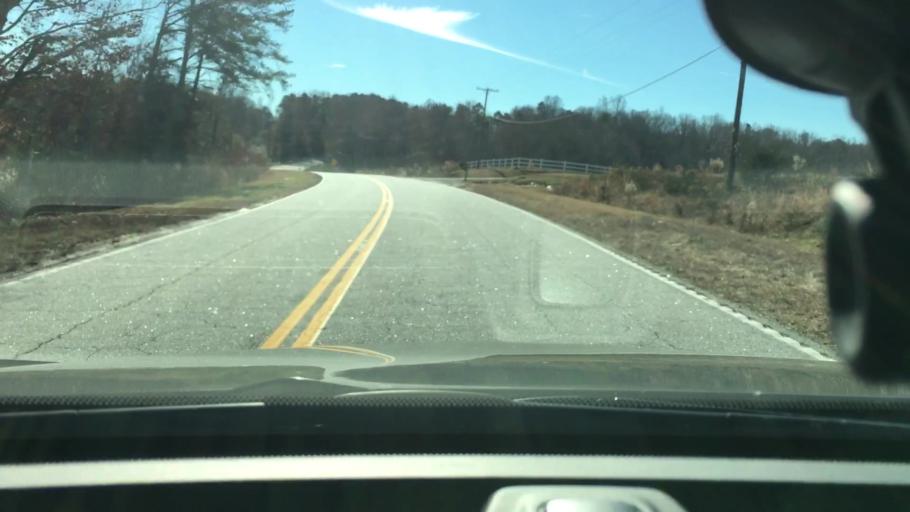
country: US
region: South Carolina
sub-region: Spartanburg County
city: Pacolet
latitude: 34.9687
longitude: -81.7054
